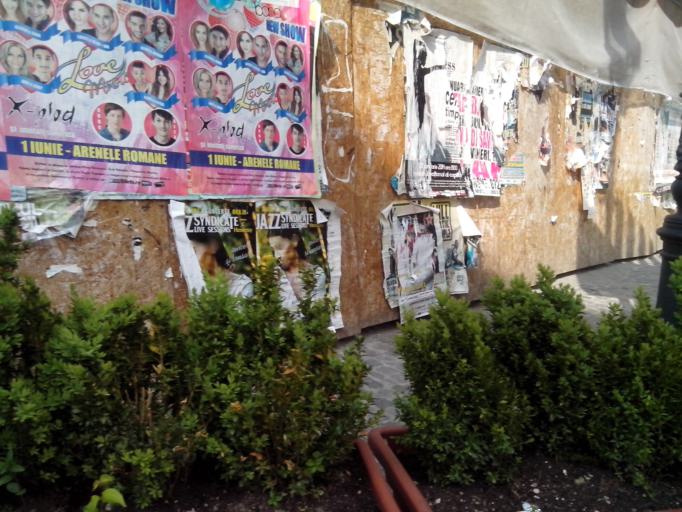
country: RO
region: Bucuresti
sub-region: Municipiul Bucuresti
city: Bucuresti
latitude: 44.4299
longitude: 26.1005
